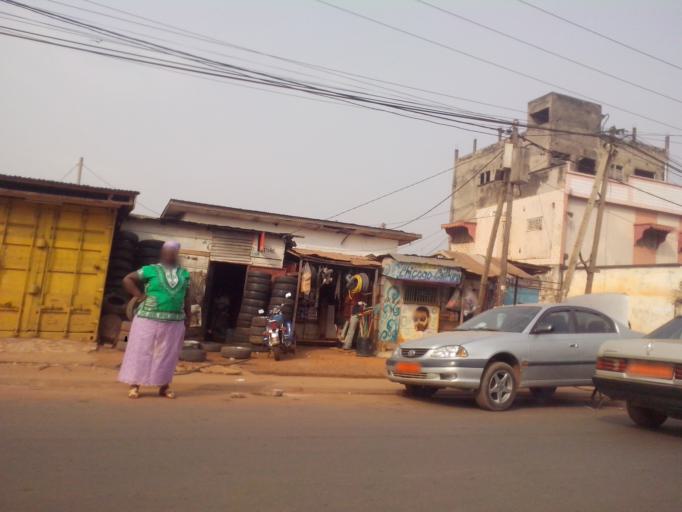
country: CM
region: Centre
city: Yaounde
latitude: 3.8469
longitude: 11.4968
